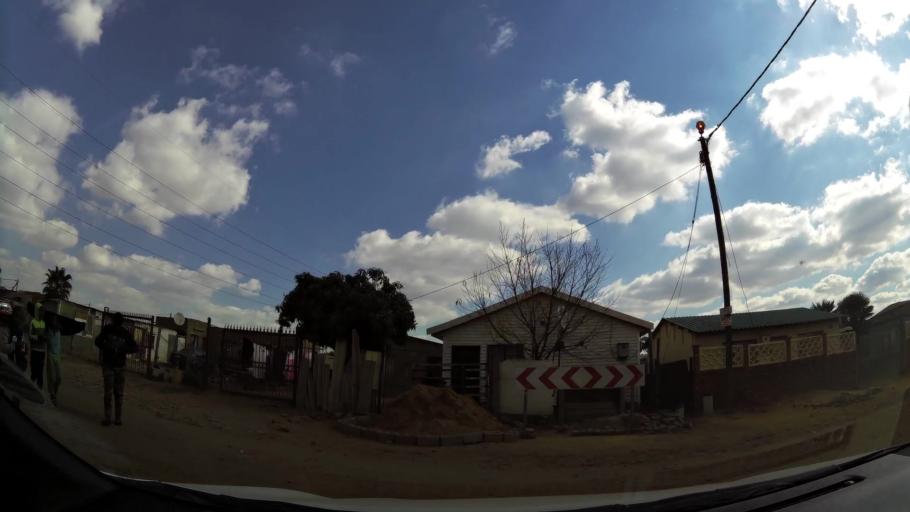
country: ZA
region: Gauteng
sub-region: City of Tshwane Metropolitan Municipality
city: Cullinan
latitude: -25.7120
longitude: 28.3993
